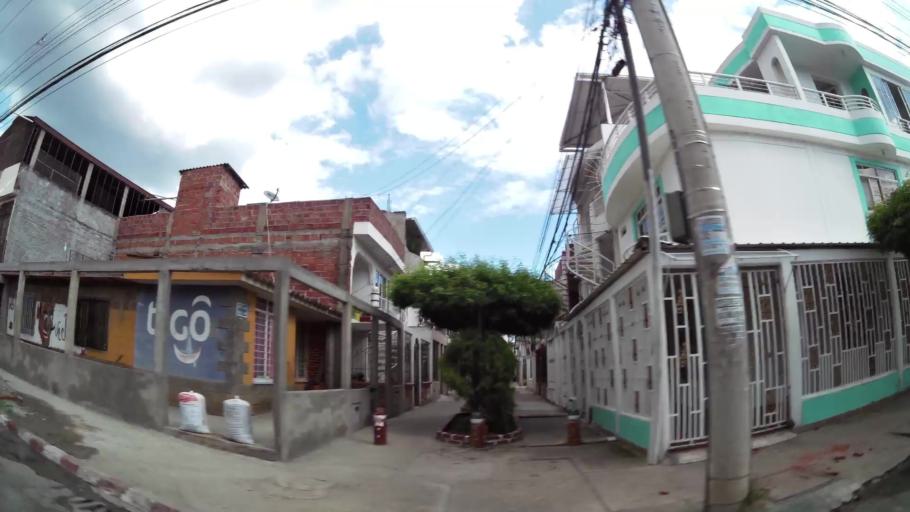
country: CO
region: Valle del Cauca
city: Cali
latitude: 3.3968
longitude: -76.5045
